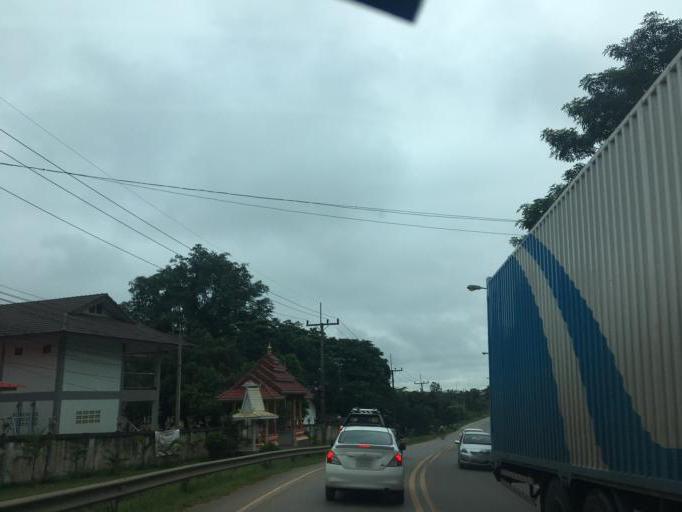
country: TH
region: Chiang Rai
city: Chiang Rai
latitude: 20.0041
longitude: 99.8760
